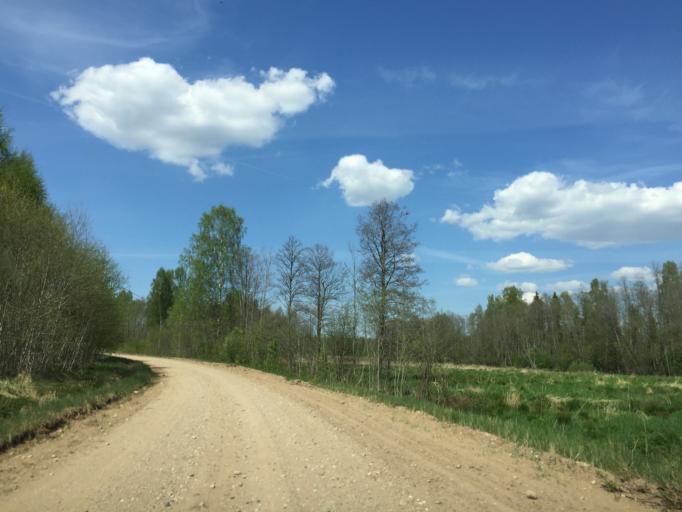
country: LV
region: Limbazu Rajons
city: Limbazi
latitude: 57.3842
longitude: 24.6093
